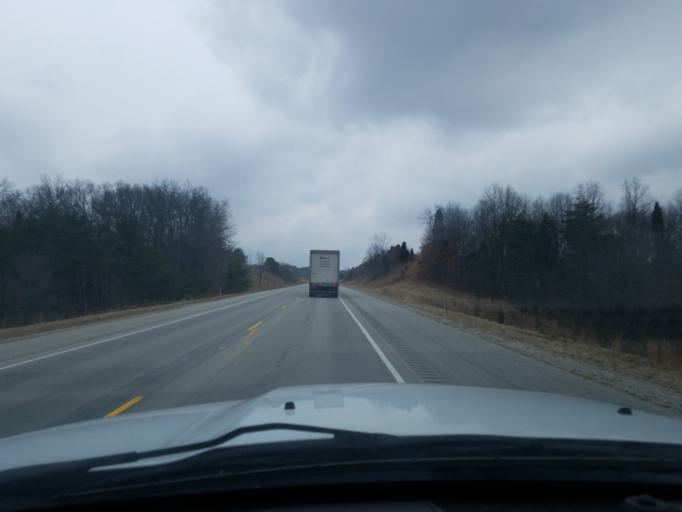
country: US
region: Indiana
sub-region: Perry County
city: Tell City
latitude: 38.0923
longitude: -86.6125
